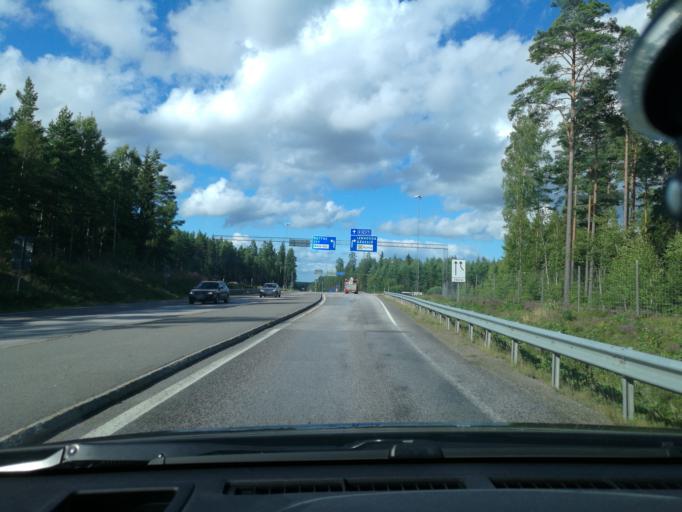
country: SE
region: Kronoberg
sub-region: Vaxjo Kommun
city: Braas
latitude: 57.0159
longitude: 15.0532
